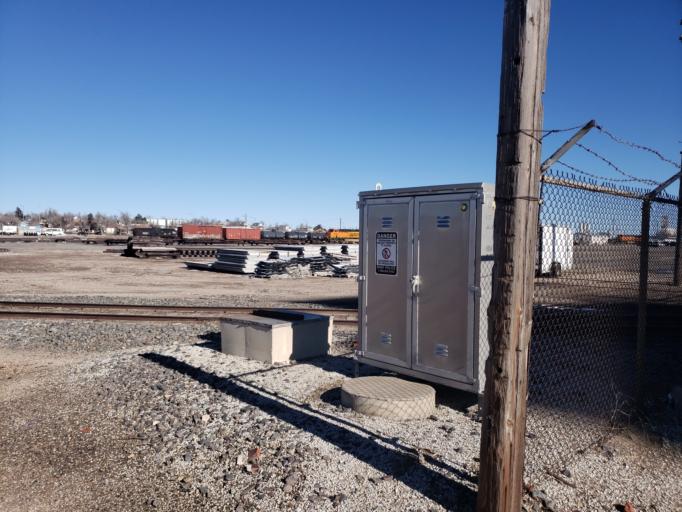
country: US
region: Kansas
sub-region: Ford County
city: Dodge City
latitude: 37.7506
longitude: -100.0100
